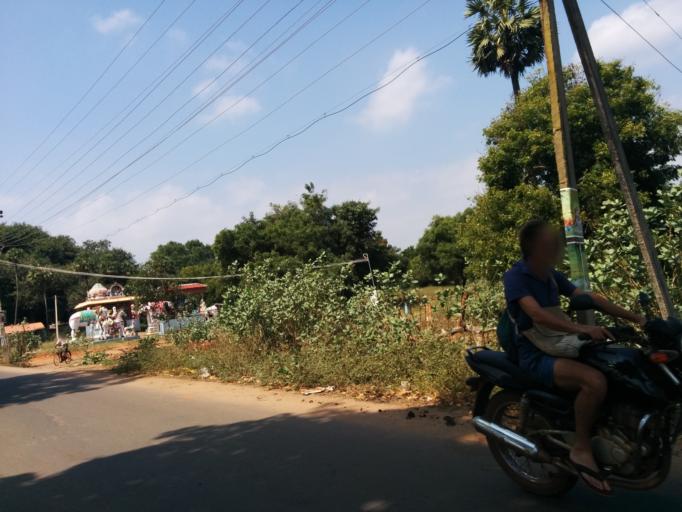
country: IN
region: Tamil Nadu
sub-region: Villupuram
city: Auroville
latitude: 11.9908
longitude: 79.8301
